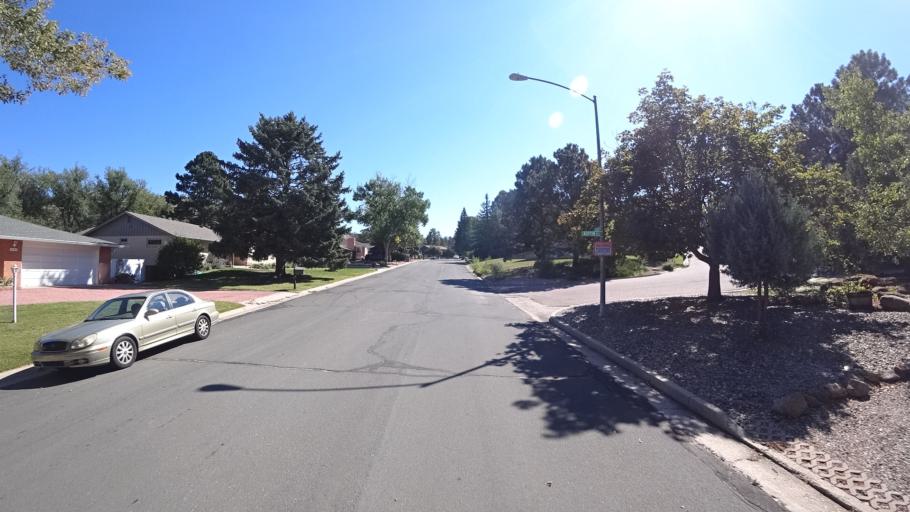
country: US
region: Colorado
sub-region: El Paso County
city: Colorado Springs
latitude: 38.8770
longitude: -104.7810
